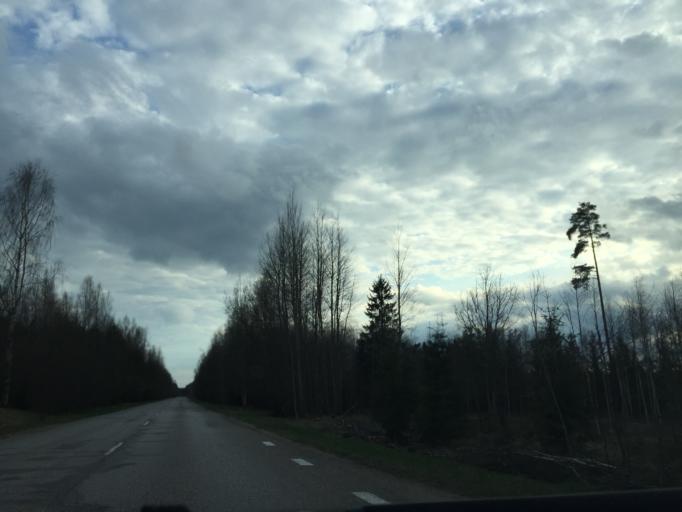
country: LV
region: Aluksnes Rajons
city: Aluksne
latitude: 57.2967
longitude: 27.0643
